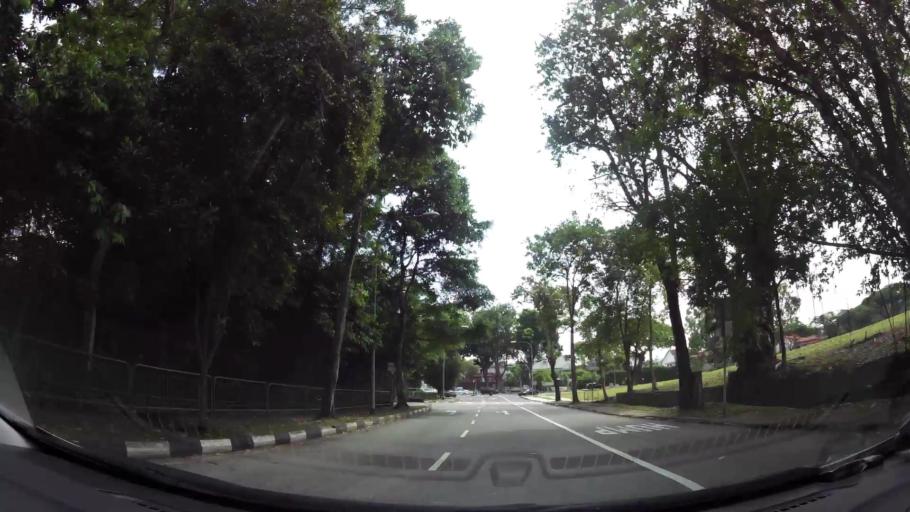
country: SG
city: Singapore
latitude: 1.3326
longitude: 103.7974
